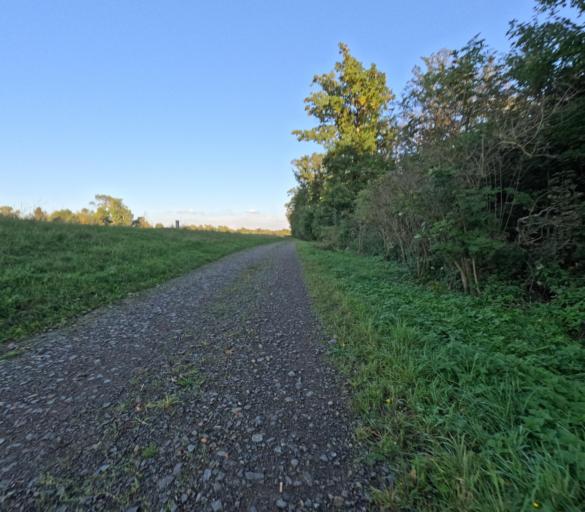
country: DE
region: Saxony
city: Schkeuditz
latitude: 51.3709
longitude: 12.2959
